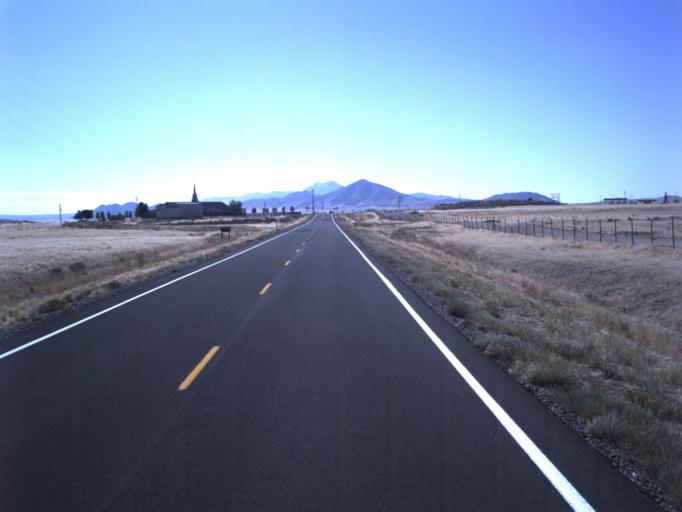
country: US
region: Utah
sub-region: Tooele County
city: Grantsville
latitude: 40.2371
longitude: -112.7233
